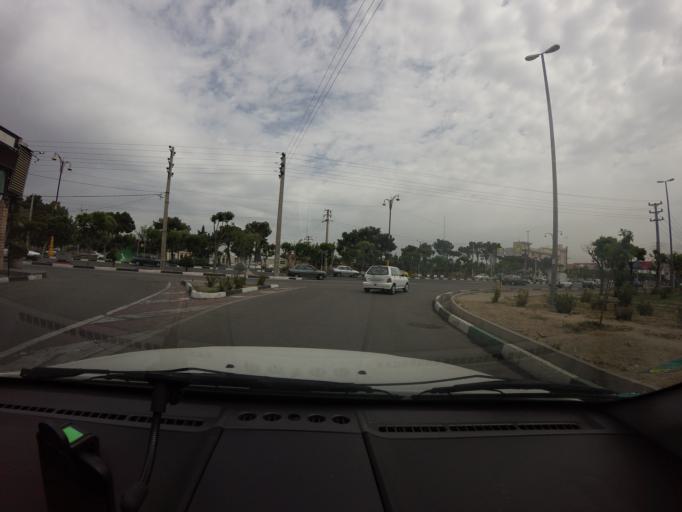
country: IR
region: Tehran
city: Eslamshahr
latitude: 35.5588
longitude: 51.2486
